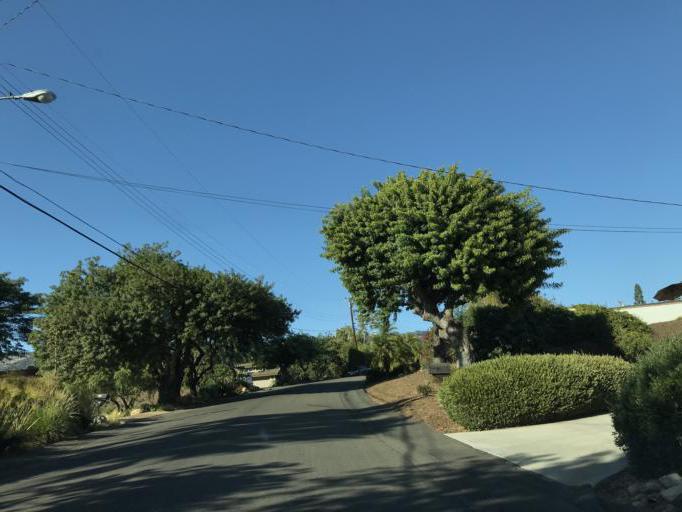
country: US
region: California
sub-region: Santa Barbara County
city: Goleta
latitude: 34.4612
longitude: -119.8212
